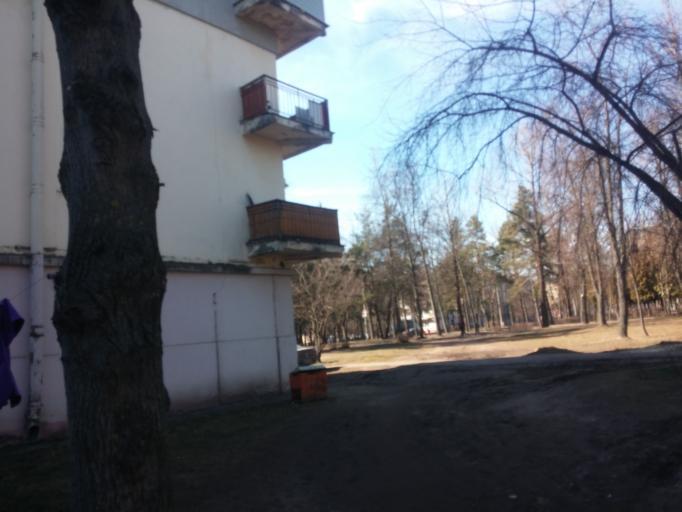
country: BY
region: Minsk
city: Vyaliki Trastsyanets
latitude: 53.8651
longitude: 27.6525
